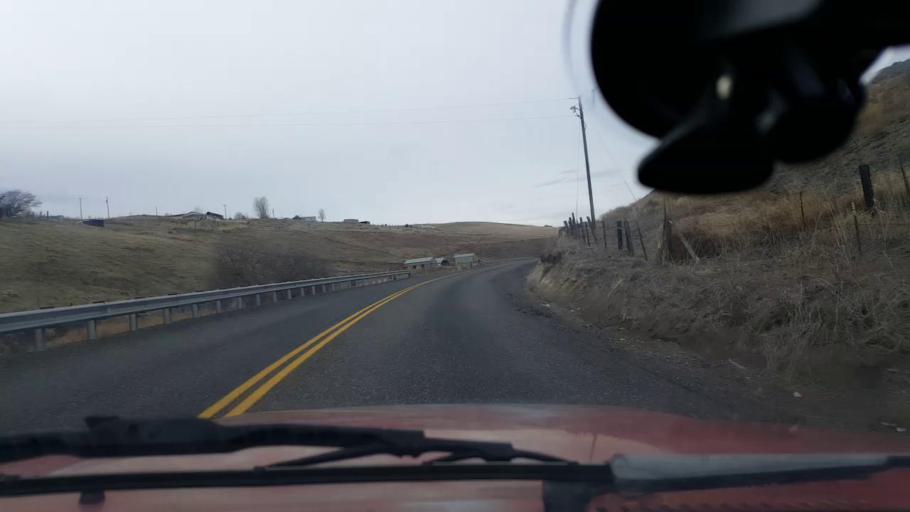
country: US
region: Washington
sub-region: Asotin County
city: Clarkston Heights-Vineland
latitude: 46.3818
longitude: -117.1224
